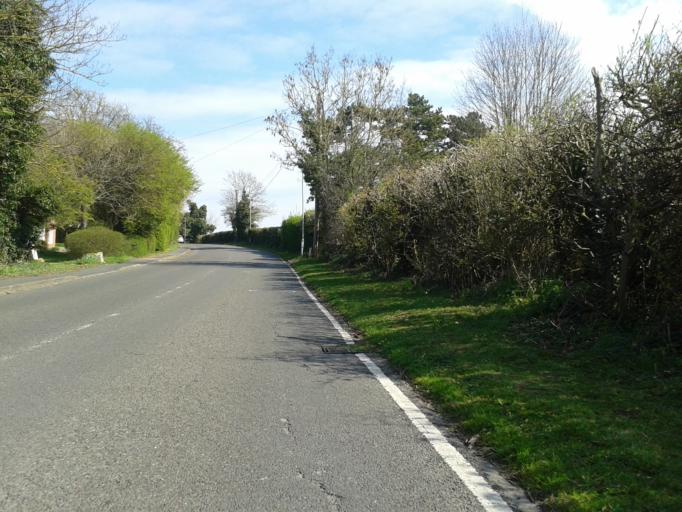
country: GB
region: England
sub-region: Cambridgeshire
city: Sawston
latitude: 52.1567
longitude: 0.1530
